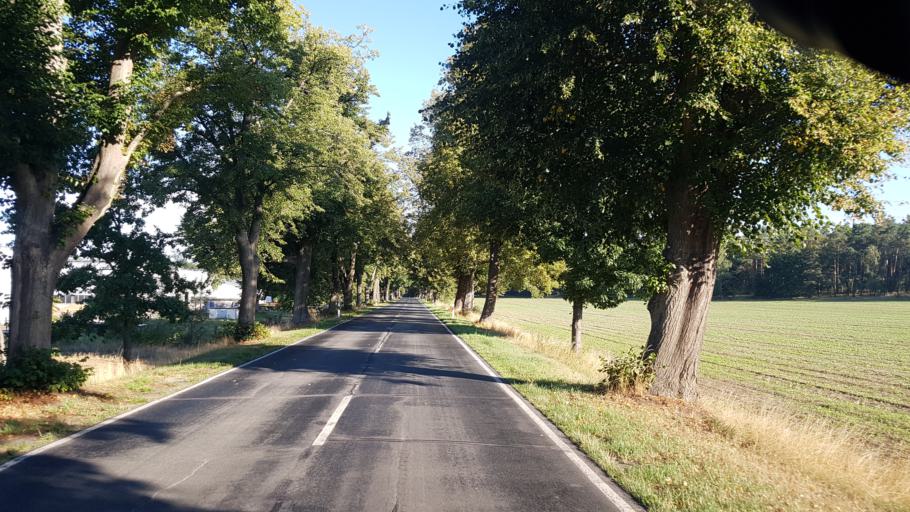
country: DE
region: Brandenburg
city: Bronkow
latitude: 51.6574
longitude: 13.9204
